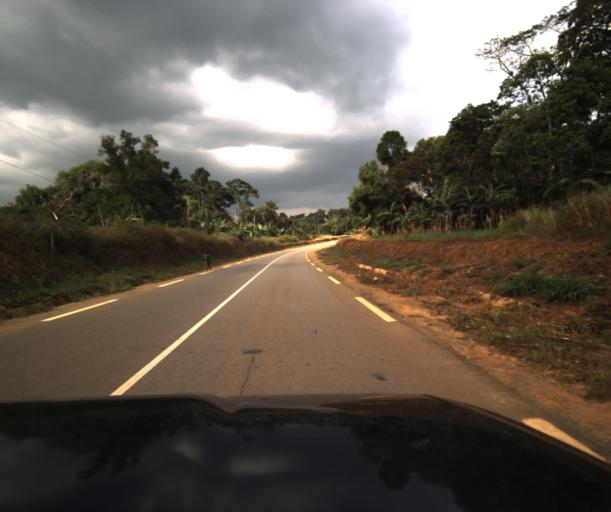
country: CM
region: Centre
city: Mbankomo
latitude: 3.6501
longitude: 11.3324
